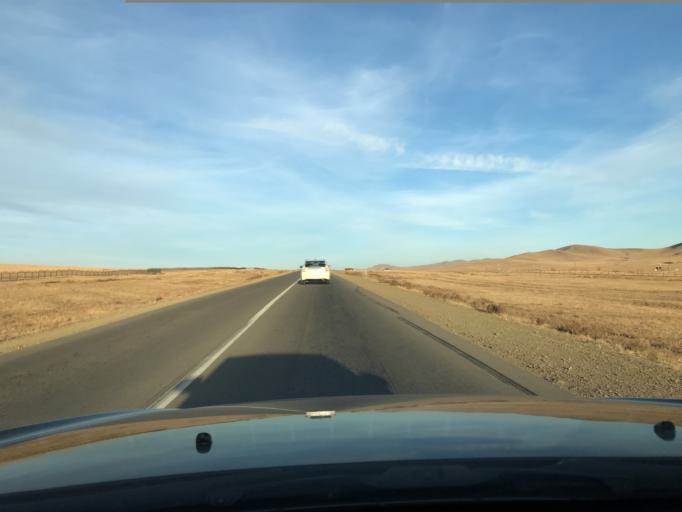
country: MN
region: Central Aimak
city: Arhust
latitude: 47.7960
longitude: 107.5006
